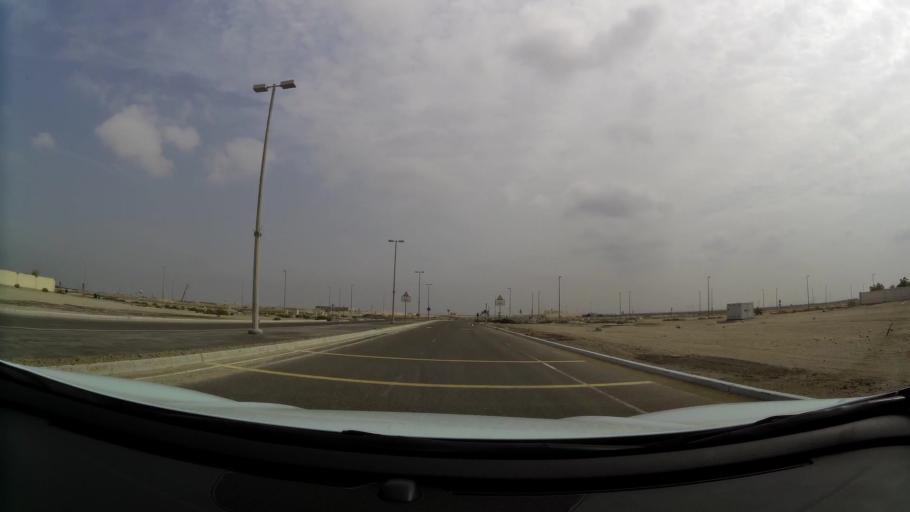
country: AE
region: Abu Dhabi
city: Abu Dhabi
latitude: 24.6065
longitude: 54.6458
